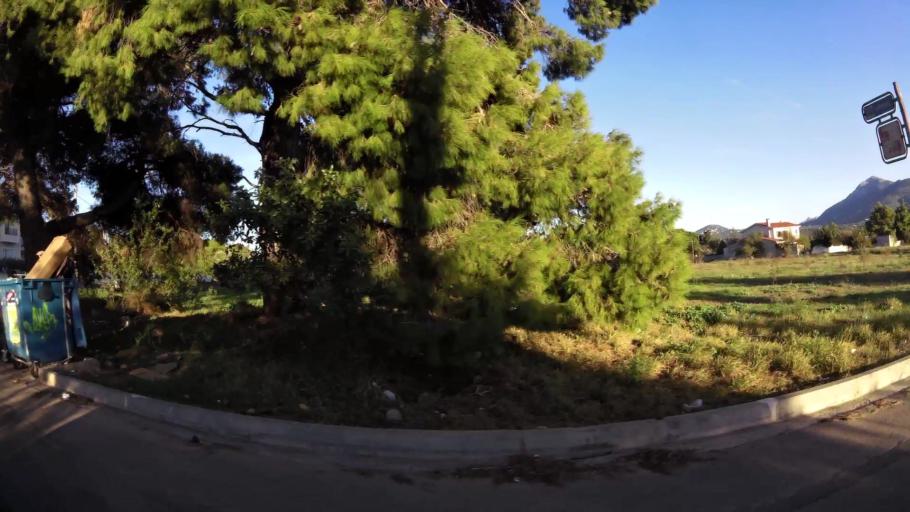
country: GR
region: Attica
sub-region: Nomarchia Anatolikis Attikis
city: Kryoneri
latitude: 38.1326
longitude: 23.8246
